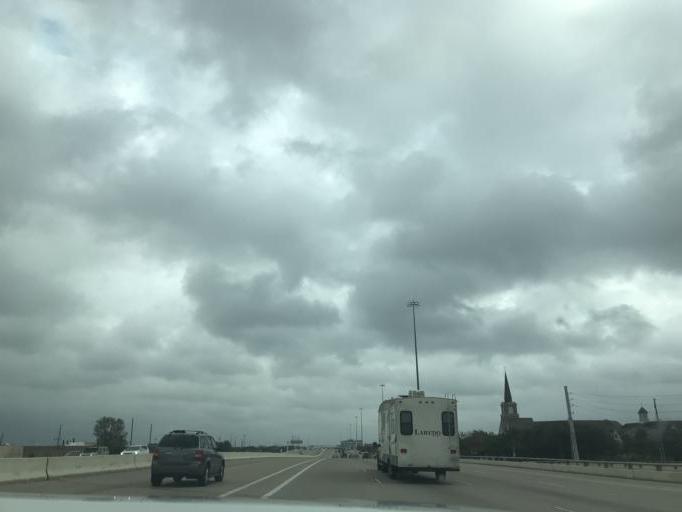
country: US
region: Texas
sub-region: Fort Bend County
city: Sugar Land
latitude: 29.5855
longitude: -95.6403
